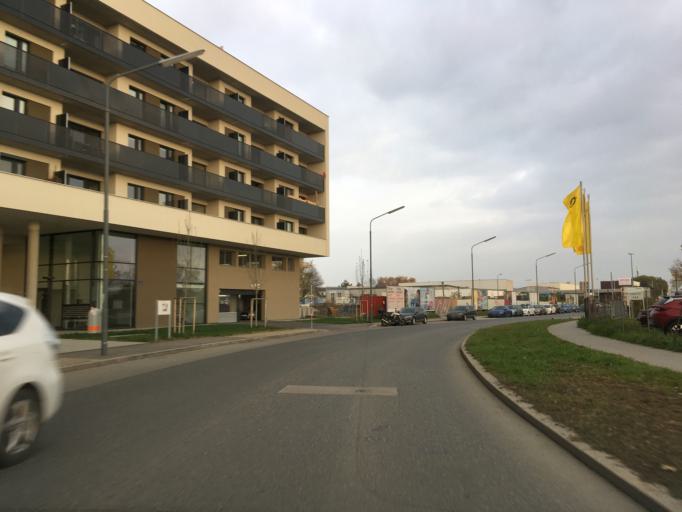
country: AT
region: Lower Austria
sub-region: Politischer Bezirk Wien-Umgebung
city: Gerasdorf bei Wien
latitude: 48.2524
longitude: 16.4602
